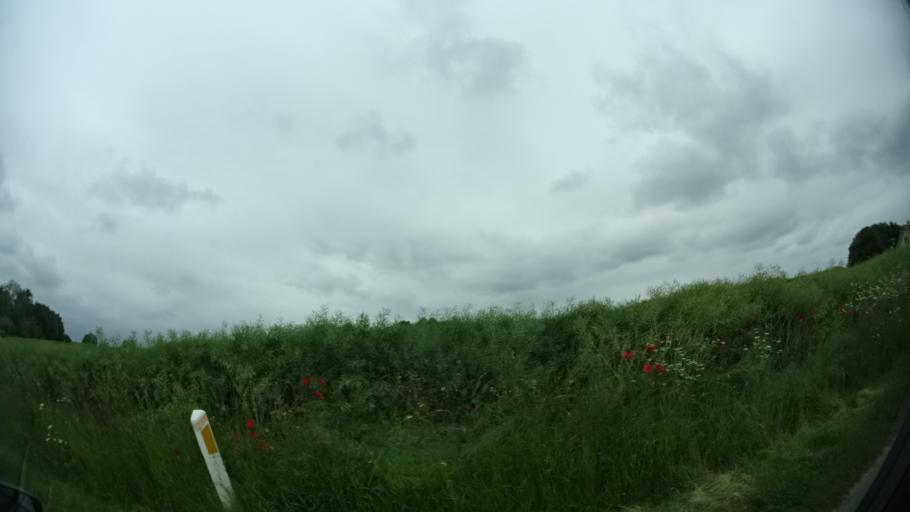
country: DK
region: Central Jutland
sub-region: Syddjurs Kommune
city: Hornslet
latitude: 56.2962
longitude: 10.3535
